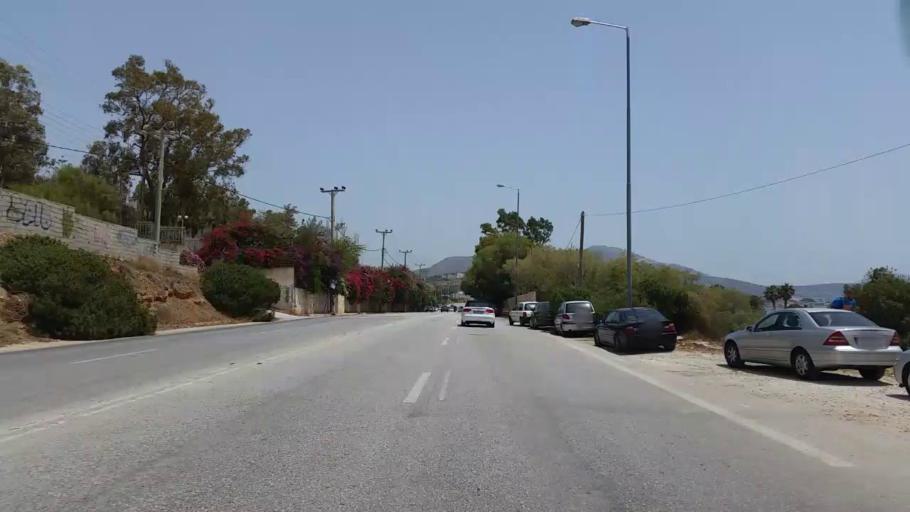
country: GR
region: Attica
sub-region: Nomarchia Anatolikis Attikis
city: Agios Dimitrios Kropias
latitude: 37.7946
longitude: 23.8743
